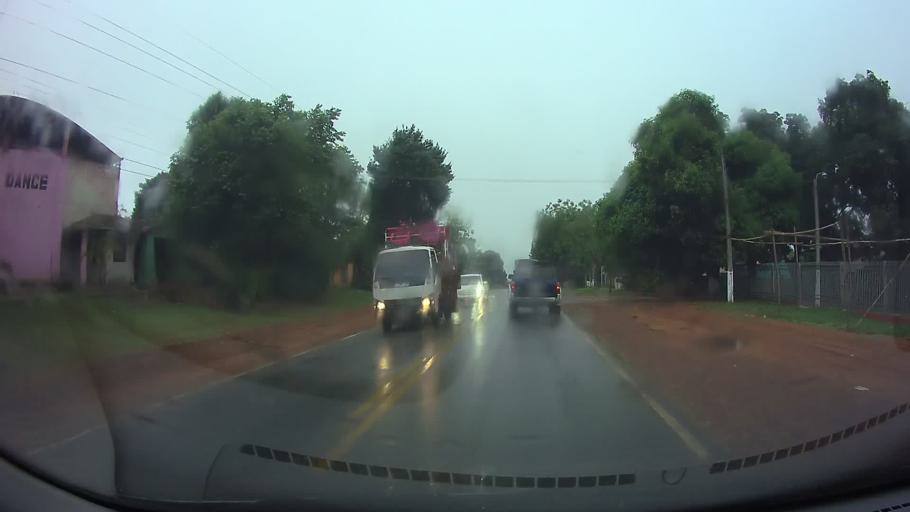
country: PY
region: Central
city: Ita
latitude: -25.4696
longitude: -57.3644
